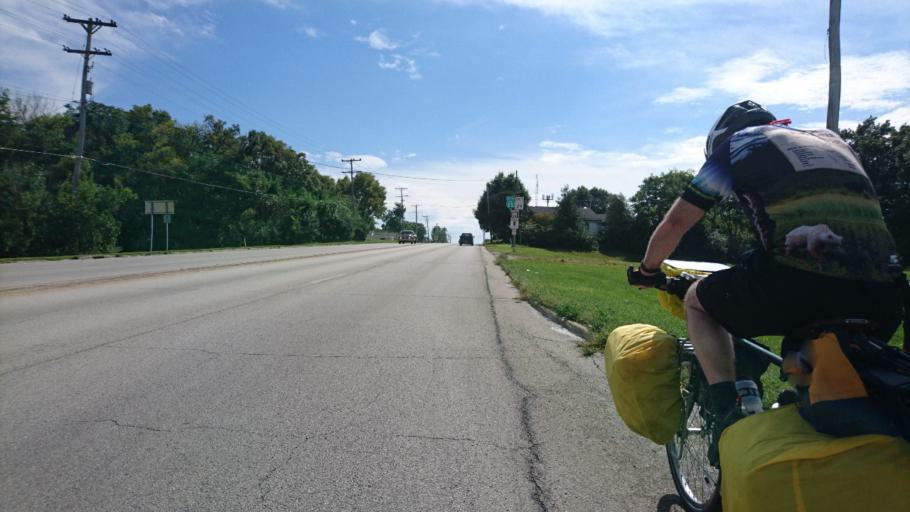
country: US
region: Illinois
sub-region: Sangamon County
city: Grandview
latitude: 39.8418
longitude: -89.6332
